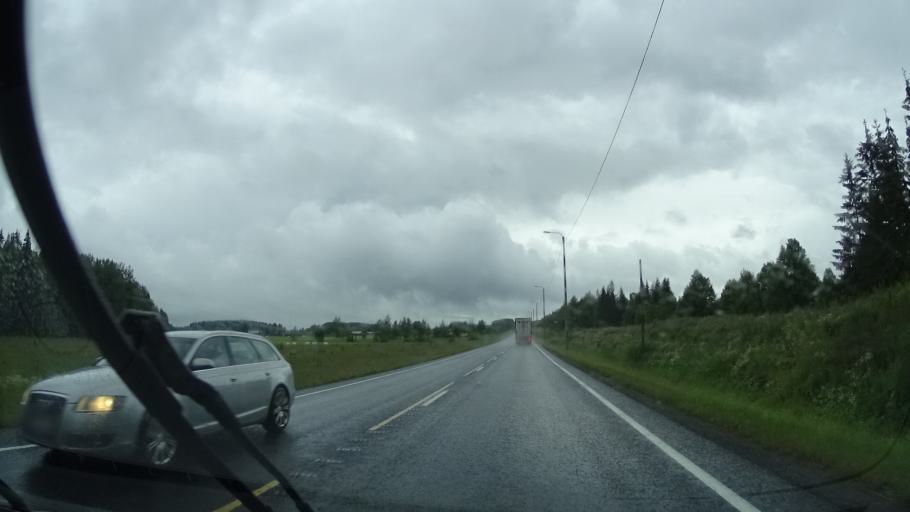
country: FI
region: Haeme
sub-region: Forssa
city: Forssa
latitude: 60.7957
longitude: 23.6336
